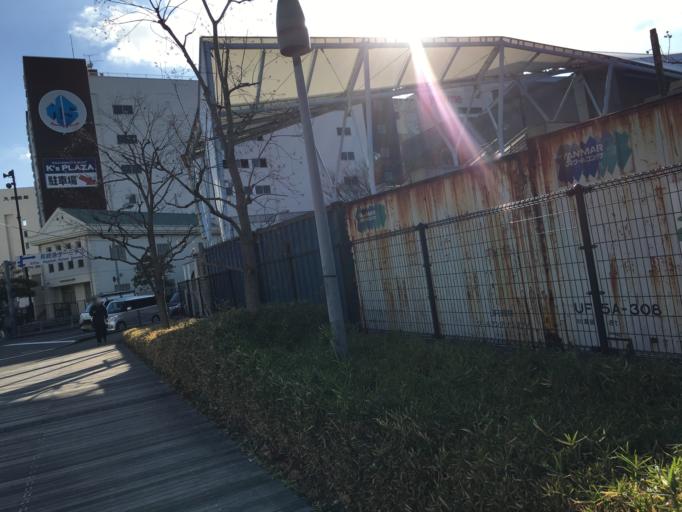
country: JP
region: Nagasaki
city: Nagasaki-shi
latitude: 32.7474
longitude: 129.8709
